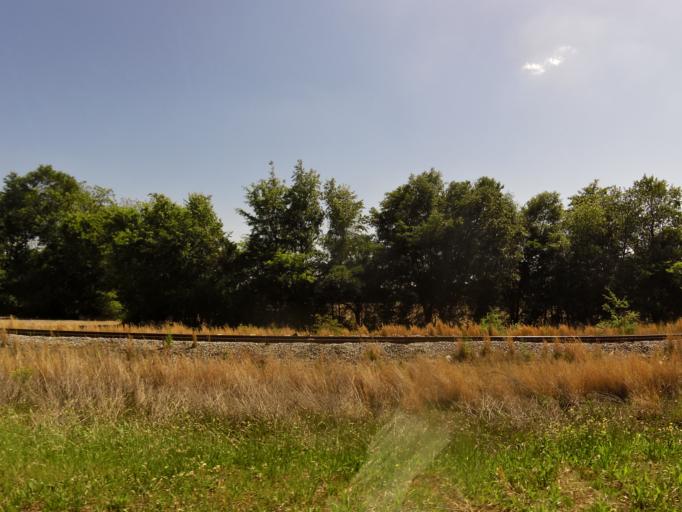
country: US
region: South Carolina
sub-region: Aiken County
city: Aiken
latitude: 33.5452
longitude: -81.6790
